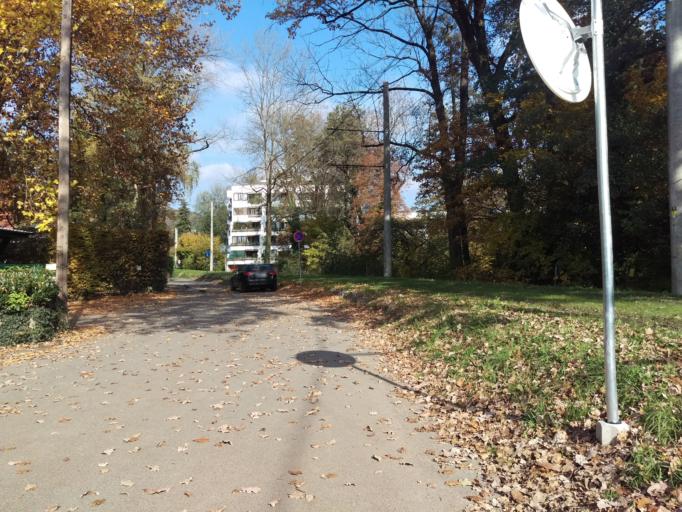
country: AT
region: Styria
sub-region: Graz Stadt
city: Graz
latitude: 47.0917
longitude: 15.4634
